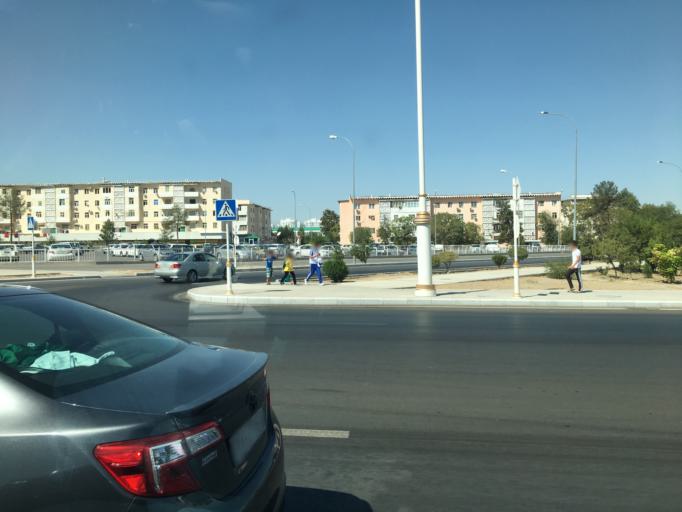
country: TM
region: Ahal
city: Ashgabat
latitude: 37.9079
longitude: 58.3891
